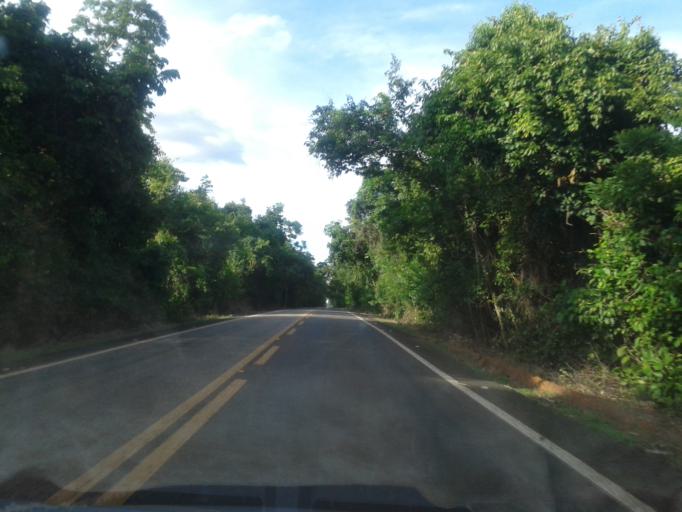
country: BR
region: Goias
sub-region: Crixas
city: Crixas
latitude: -13.9767
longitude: -50.3221
